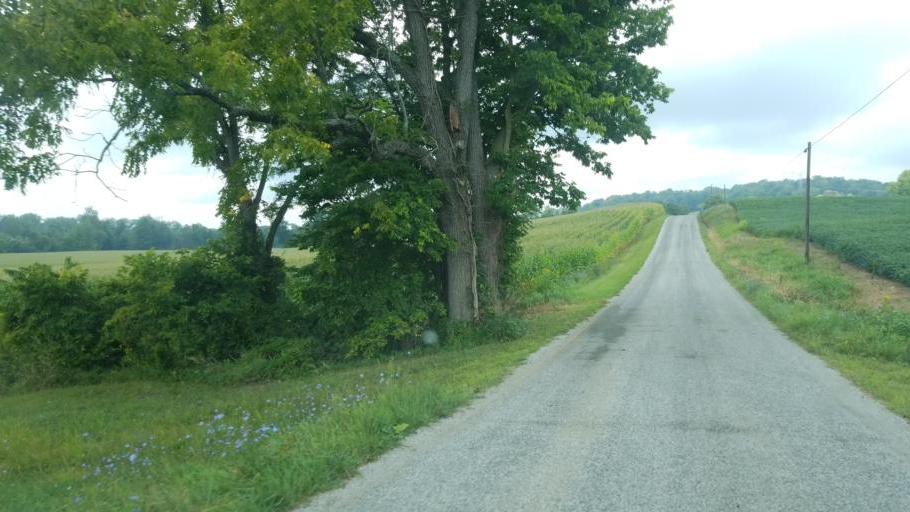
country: US
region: Ohio
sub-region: Licking County
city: Utica
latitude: 40.2092
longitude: -82.4672
